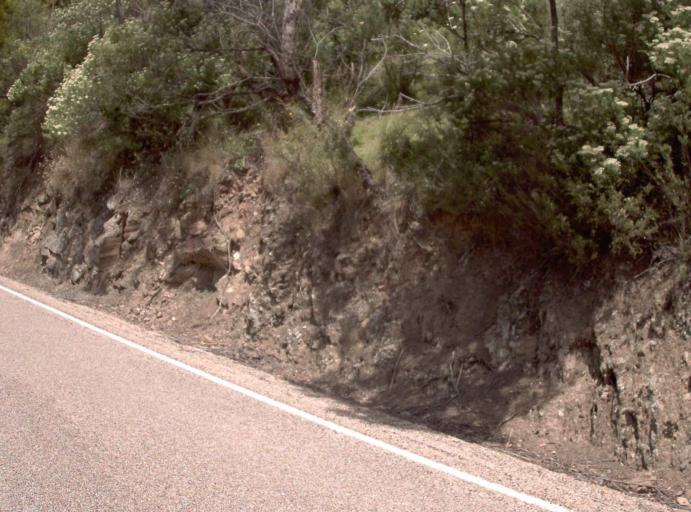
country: AU
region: Victoria
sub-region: East Gippsland
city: Lakes Entrance
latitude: -37.5464
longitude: 147.8663
